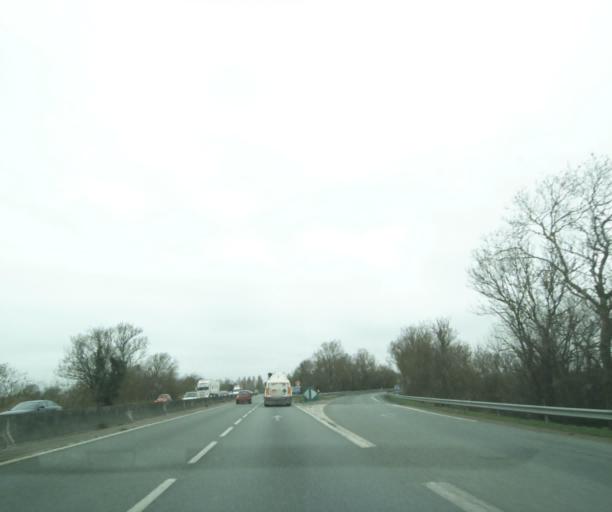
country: FR
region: Poitou-Charentes
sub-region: Departement de la Charente-Maritime
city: Angoulins
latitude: 46.1189
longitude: -1.1078
